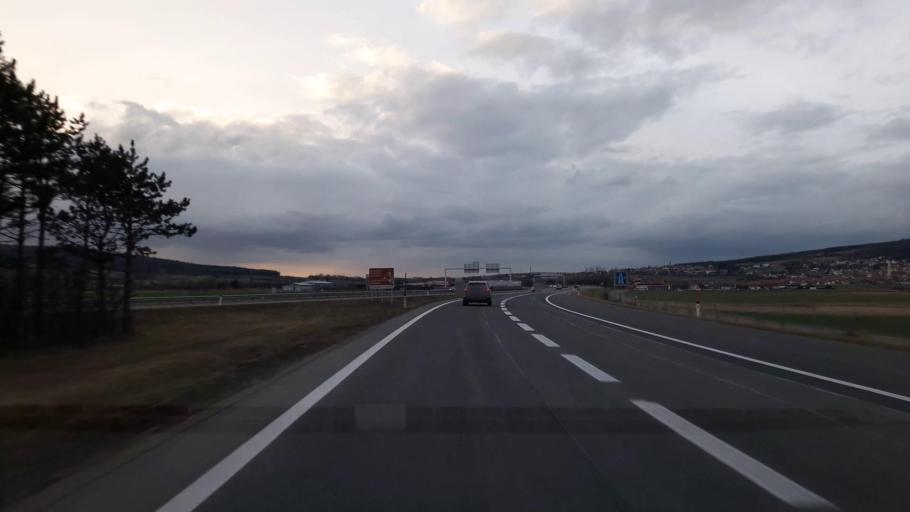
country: AT
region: Burgenland
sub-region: Eisenstadt-Umgebung
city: Wulkaprodersdorf
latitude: 47.8188
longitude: 16.4929
